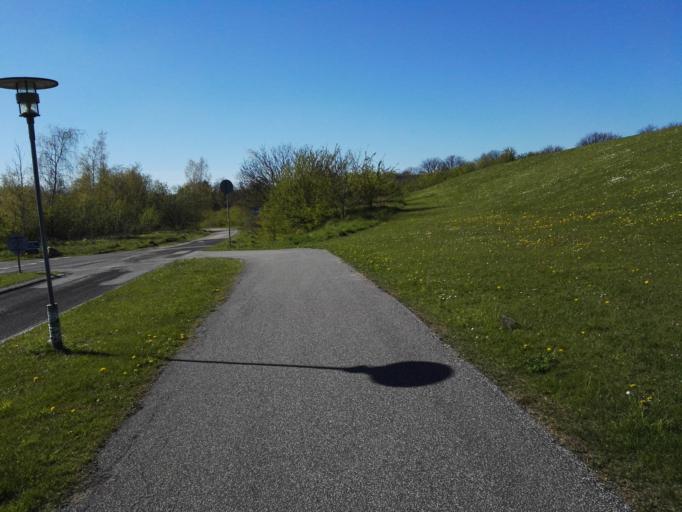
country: DK
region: Capital Region
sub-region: Egedal Kommune
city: Vekso
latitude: 55.7525
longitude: 12.2307
